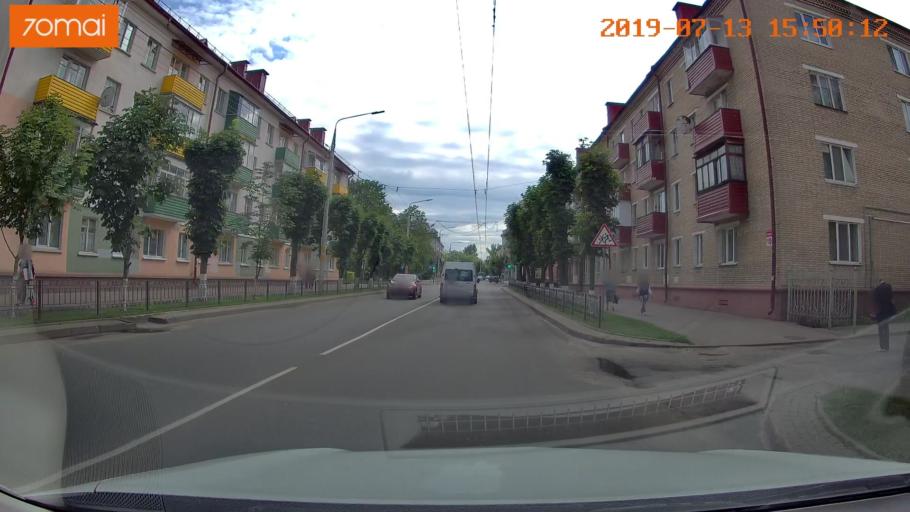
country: BY
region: Mogilev
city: Babruysk
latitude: 53.1440
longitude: 29.2261
